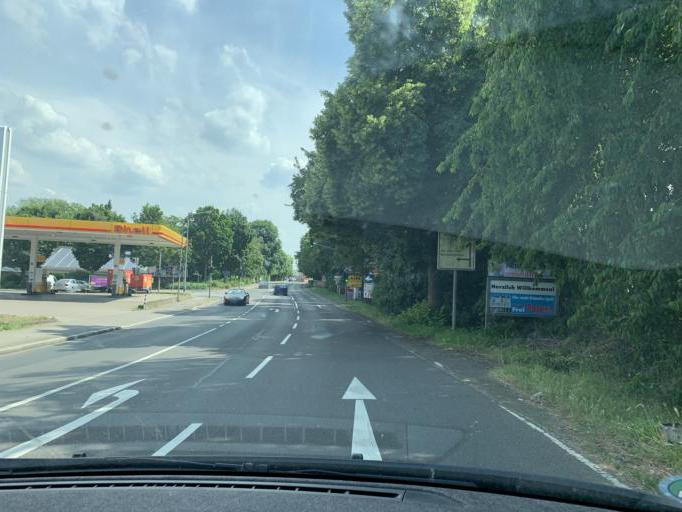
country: DE
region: North Rhine-Westphalia
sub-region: Regierungsbezirk Koln
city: Bedburg
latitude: 50.9968
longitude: 6.5684
